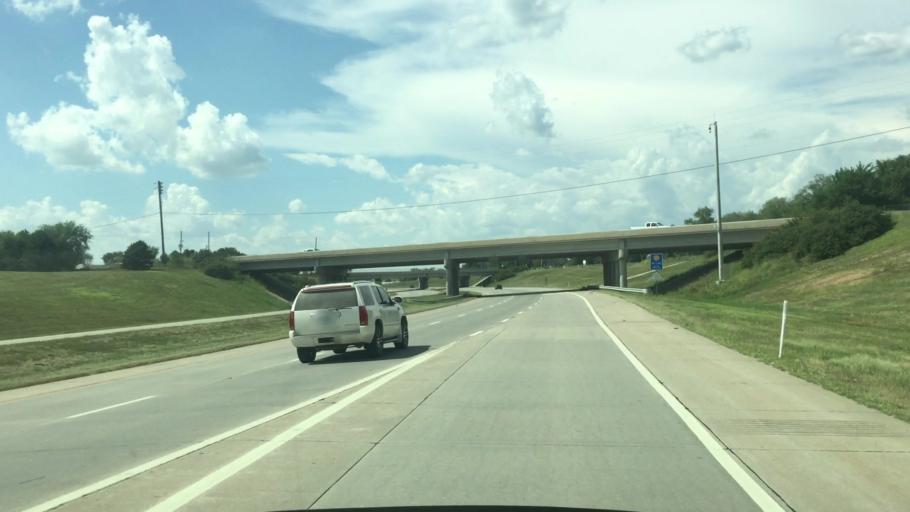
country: US
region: Kansas
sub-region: Butler County
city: Andover
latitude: 37.6930
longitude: -97.1868
